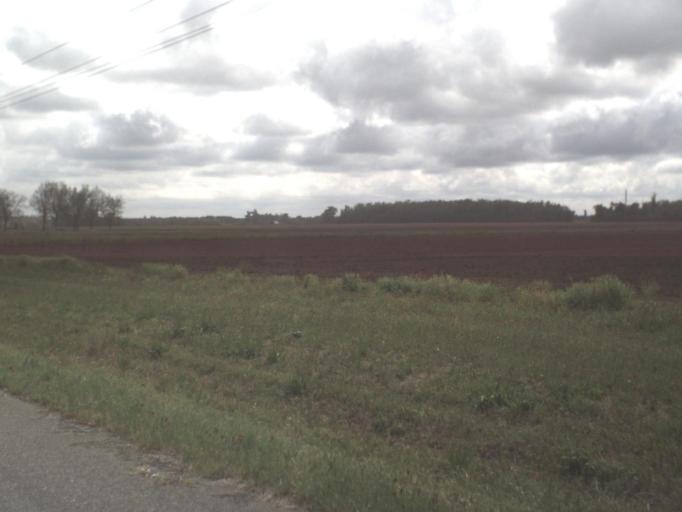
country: US
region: Florida
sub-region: Santa Rosa County
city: Point Baker
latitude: 30.7932
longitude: -87.0923
